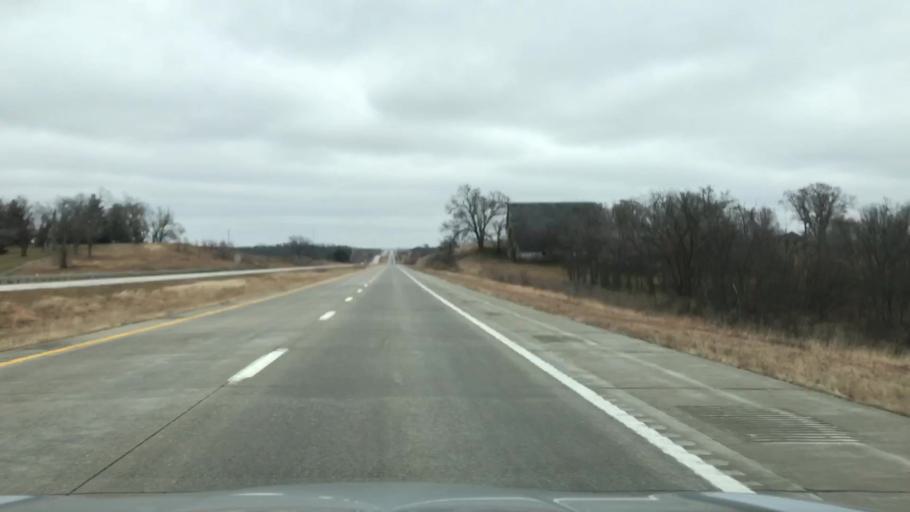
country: US
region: Missouri
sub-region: Caldwell County
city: Hamilton
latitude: 39.7350
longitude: -93.8376
